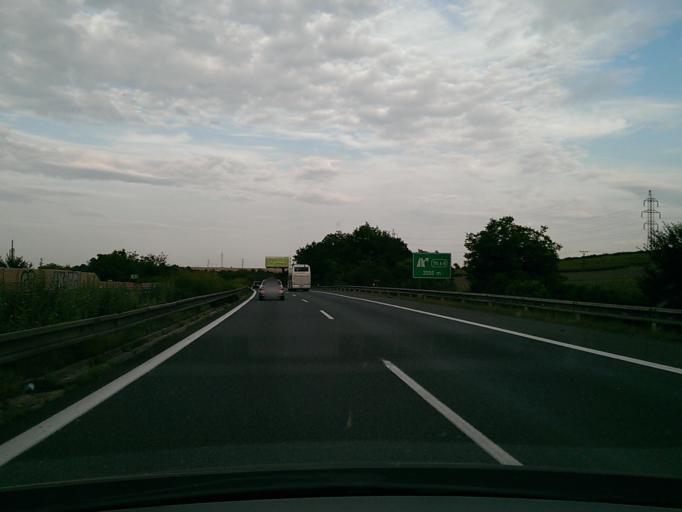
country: CZ
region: South Moravian
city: Ostopovice
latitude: 49.1616
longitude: 16.5634
